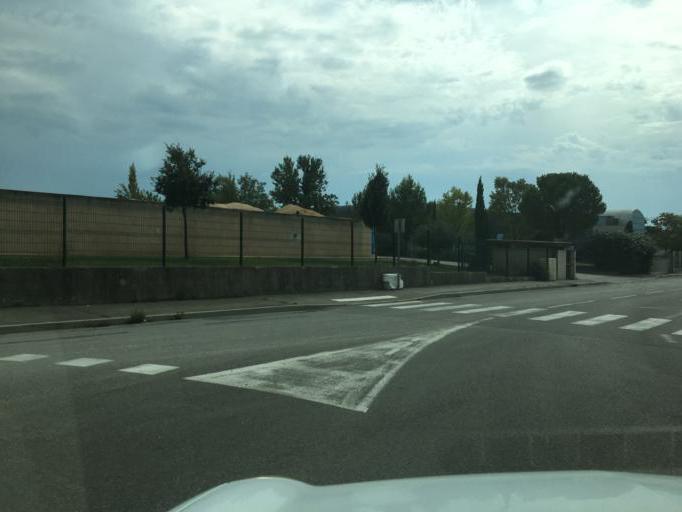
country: FR
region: Provence-Alpes-Cote d'Azur
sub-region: Departement des Bouches-du-Rhone
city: Bouc-Bel-Air
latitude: 43.4853
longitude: 5.3897
